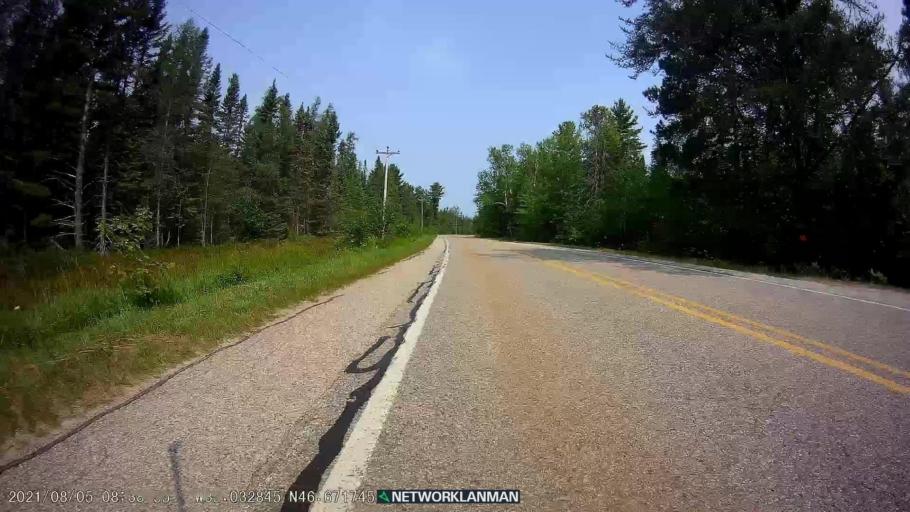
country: US
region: Michigan
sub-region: Luce County
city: Newberry
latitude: 46.6712
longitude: -85.0325
